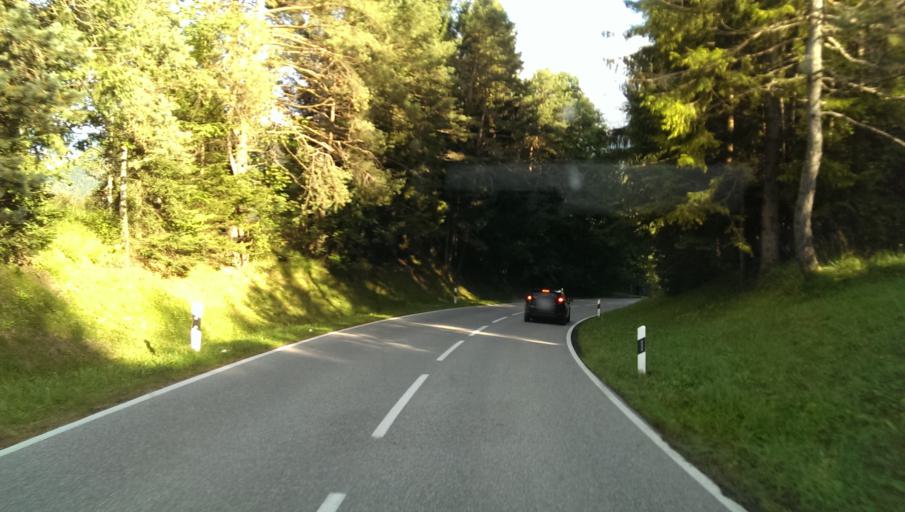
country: DE
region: Bavaria
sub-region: Upper Bavaria
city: Mittenwald
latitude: 47.4685
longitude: 11.2587
